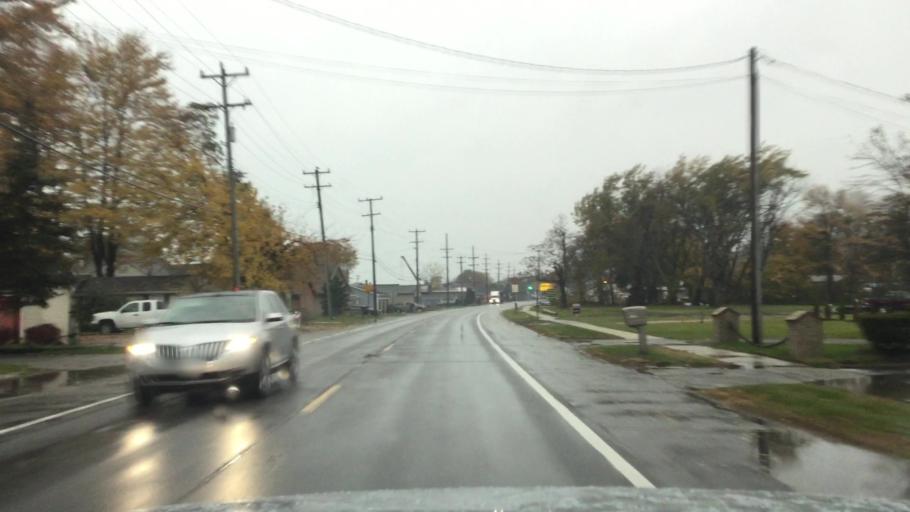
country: US
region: Michigan
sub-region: Saint Clair County
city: Algonac
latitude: 42.6177
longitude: -82.5562
